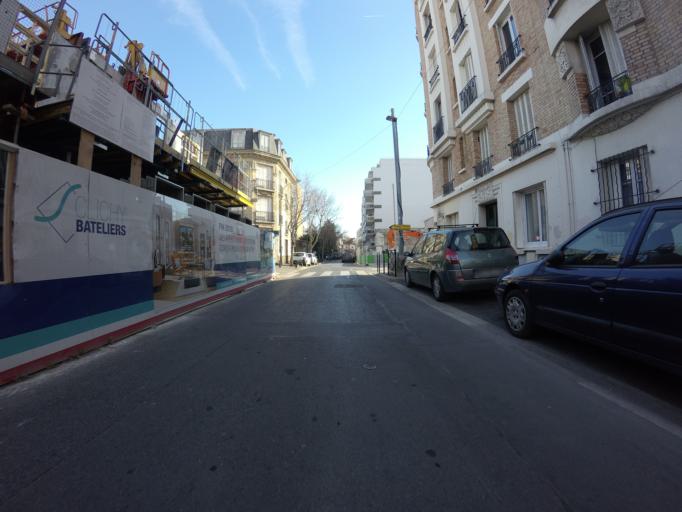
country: FR
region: Ile-de-France
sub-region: Departement des Hauts-de-Seine
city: Clichy
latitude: 48.9070
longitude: 2.3041
